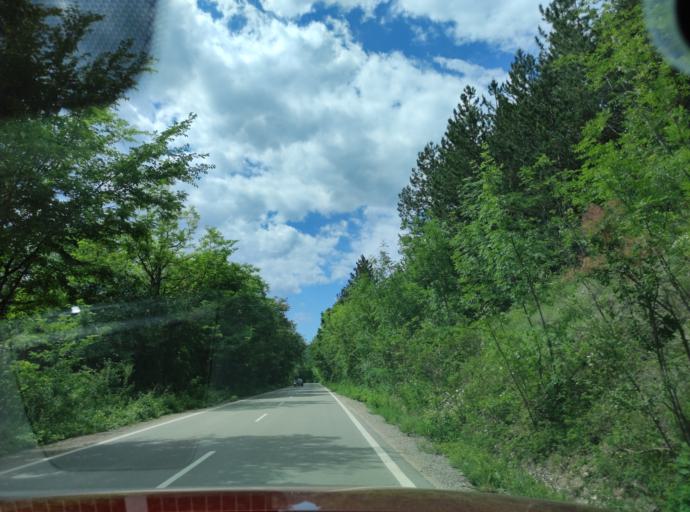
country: BG
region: Montana
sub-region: Obshtina Chiprovtsi
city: Chiprovtsi
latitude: 43.4336
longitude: 22.9596
